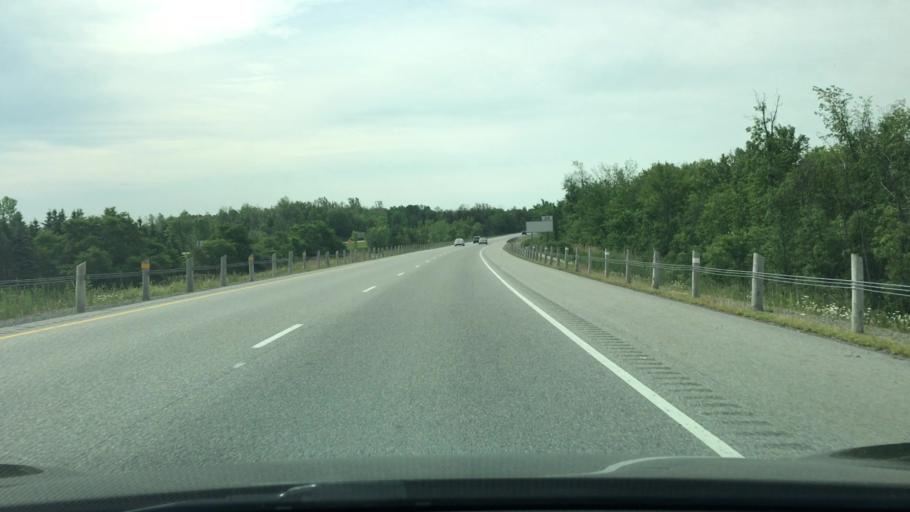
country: CA
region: Ontario
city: Prescott
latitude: 44.9991
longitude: -75.6148
